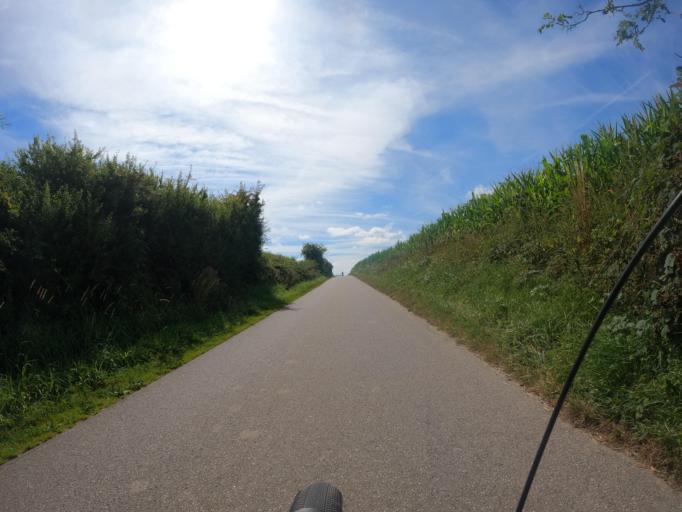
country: DE
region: Schleswig-Holstein
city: Steinbergkirche
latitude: 54.7772
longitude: 9.7599
